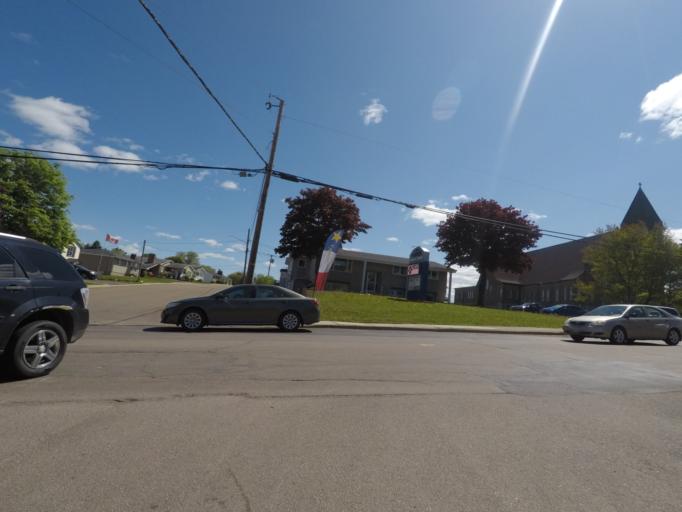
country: CA
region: New Brunswick
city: Moncton
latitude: 46.0971
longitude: -64.7538
